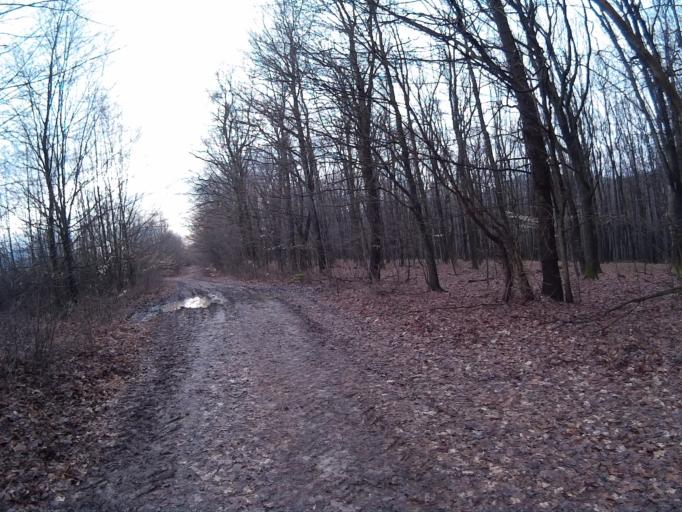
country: HU
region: Borsod-Abauj-Zemplen
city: Satoraljaujhely
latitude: 48.4143
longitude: 21.5981
